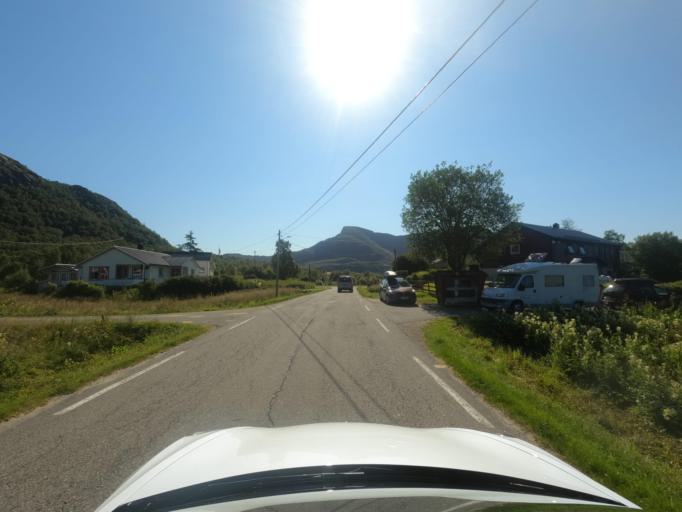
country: NO
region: Nordland
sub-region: Hadsel
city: Stokmarknes
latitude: 68.3092
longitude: 14.9930
